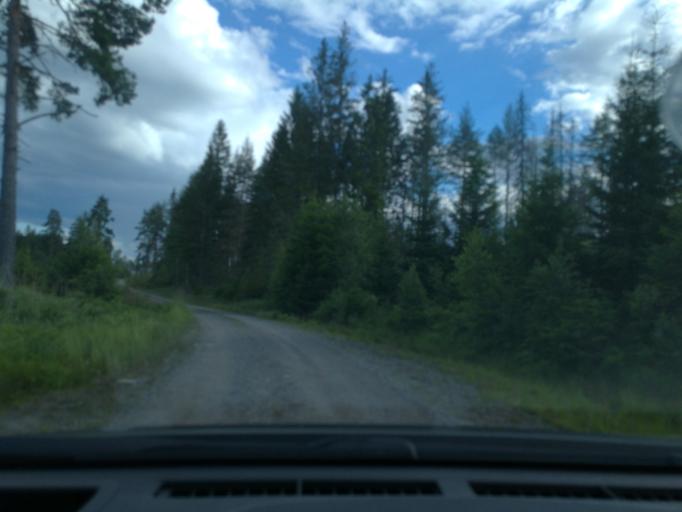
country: SE
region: Vaestmanland
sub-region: Surahammars Kommun
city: Ramnas
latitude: 59.8390
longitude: 16.2754
